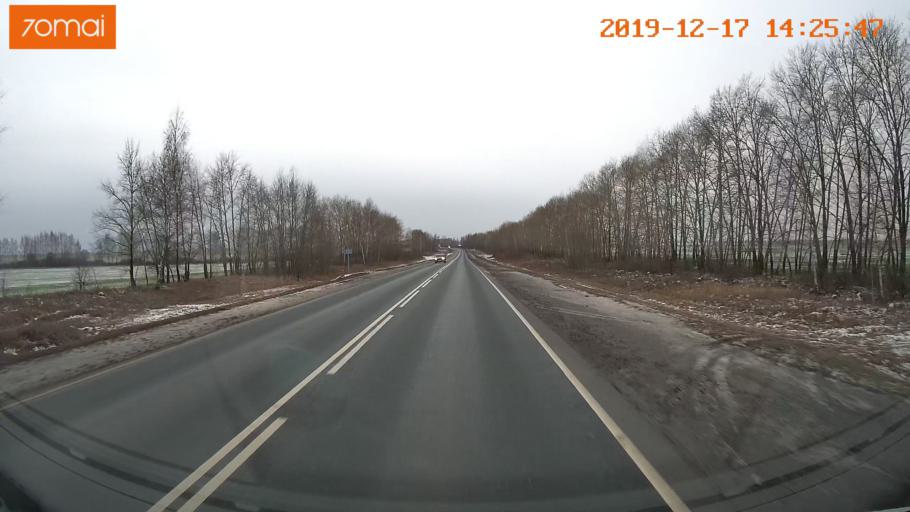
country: RU
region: Rjazan
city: Zakharovo
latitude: 54.3896
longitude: 39.3228
